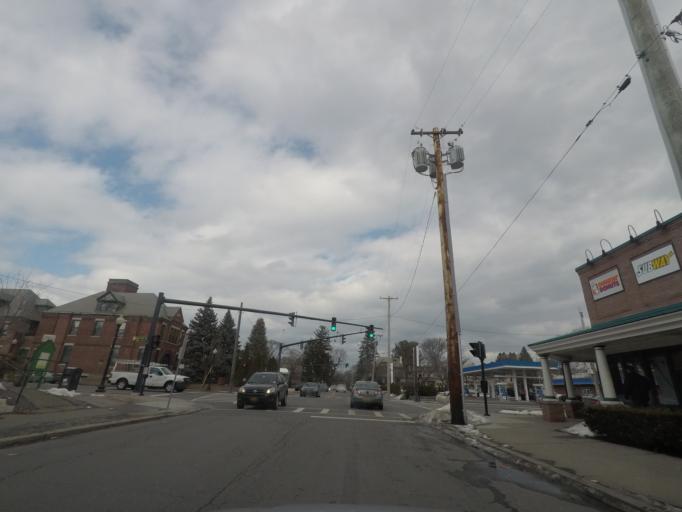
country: US
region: New York
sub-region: Albany County
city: West Albany
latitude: 42.6653
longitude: -73.7908
